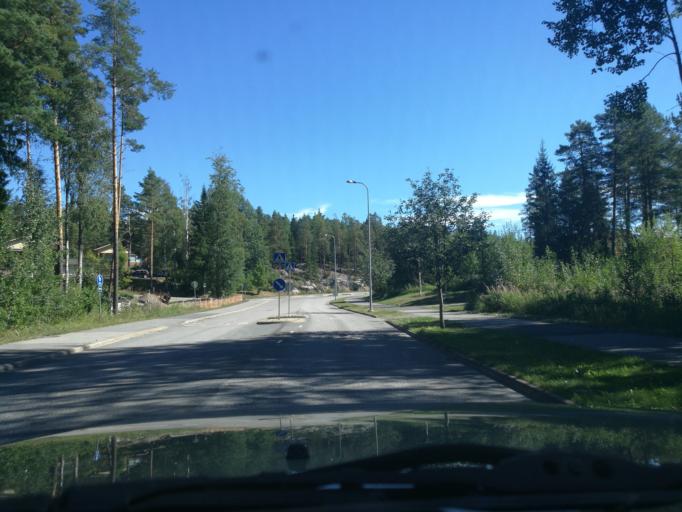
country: FI
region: Uusimaa
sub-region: Helsinki
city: Kerava
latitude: 60.3570
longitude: 25.1349
